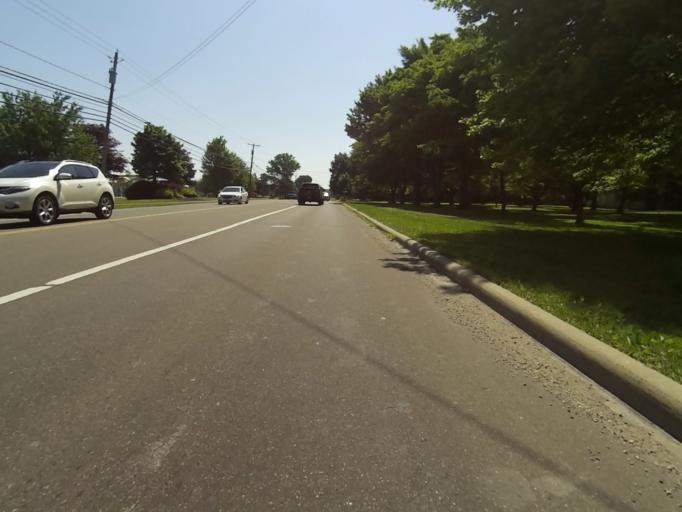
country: US
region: Ohio
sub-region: Summit County
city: Stow
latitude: 41.1663
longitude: -81.4000
